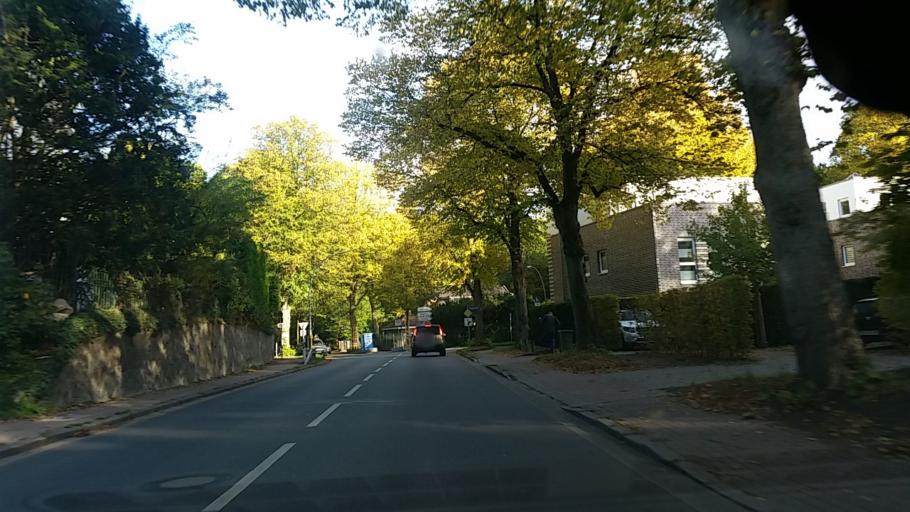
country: DE
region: Hamburg
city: Duvenstedt
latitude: 53.7047
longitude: 10.1192
